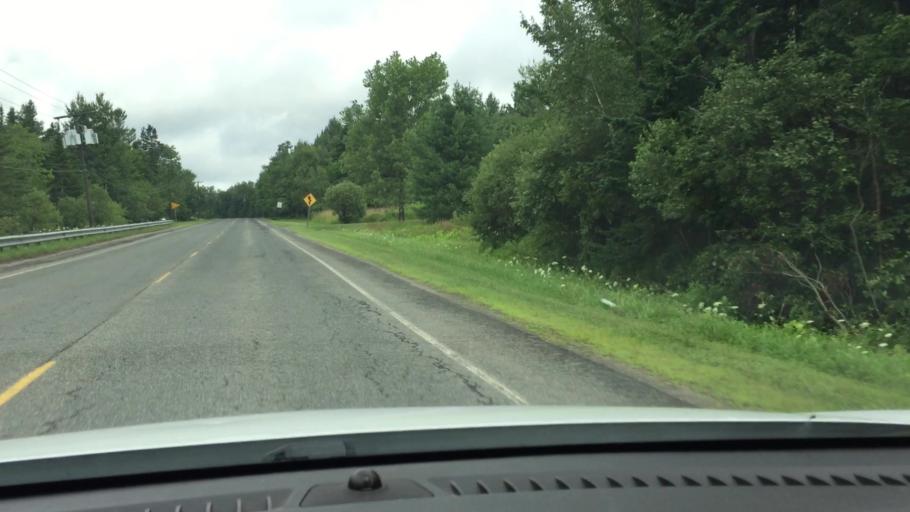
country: US
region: Massachusetts
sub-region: Berkshire County
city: Hinsdale
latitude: 42.4430
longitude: -73.0528
